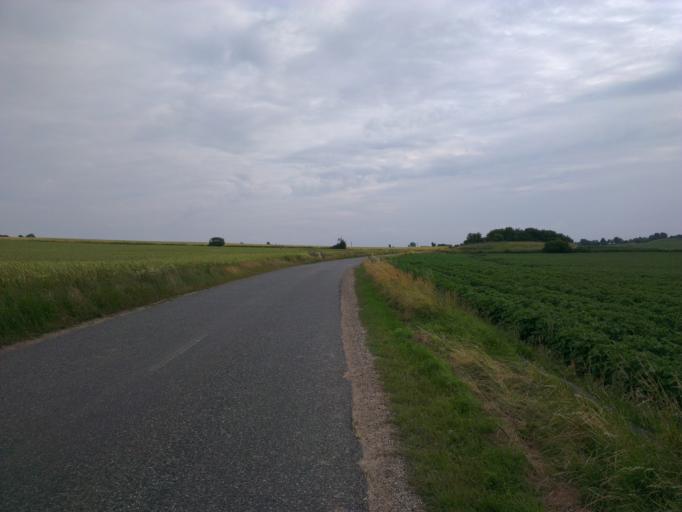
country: DK
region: Capital Region
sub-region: Frederikssund Kommune
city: Skibby
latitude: 55.8034
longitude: 11.9312
